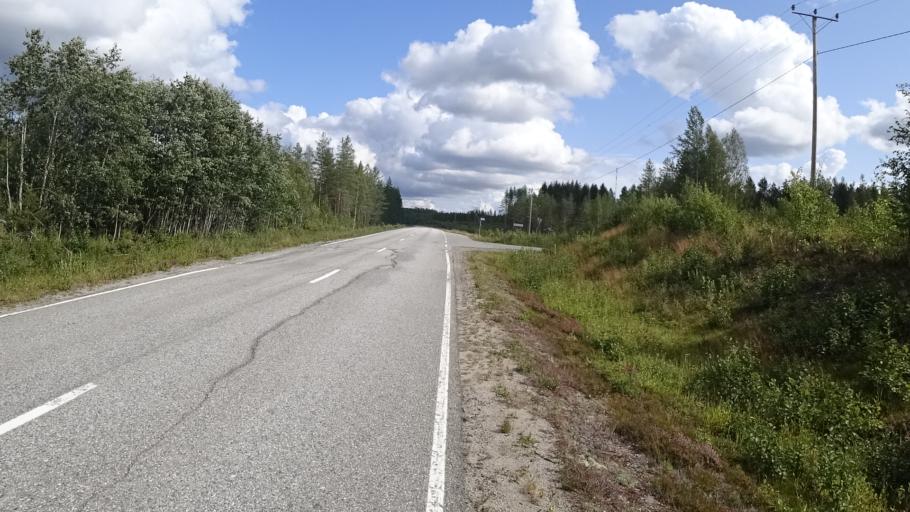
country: FI
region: North Karelia
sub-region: Joensuu
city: Ilomantsi
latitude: 62.6192
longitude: 31.2208
